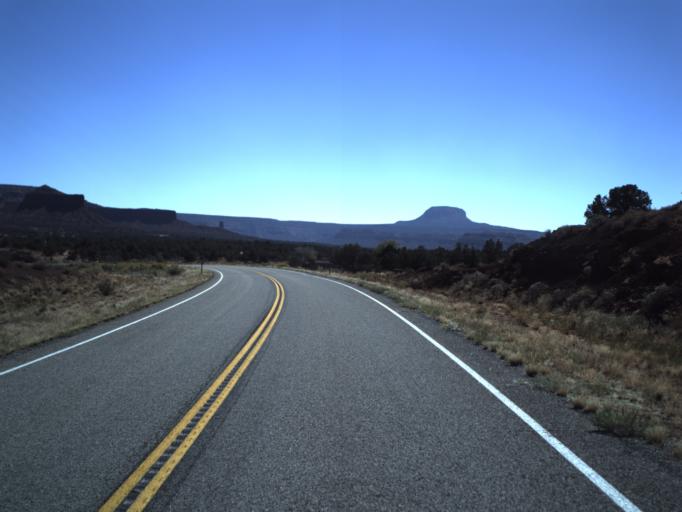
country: US
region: Utah
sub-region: San Juan County
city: Blanding
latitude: 37.6370
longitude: -110.1591
